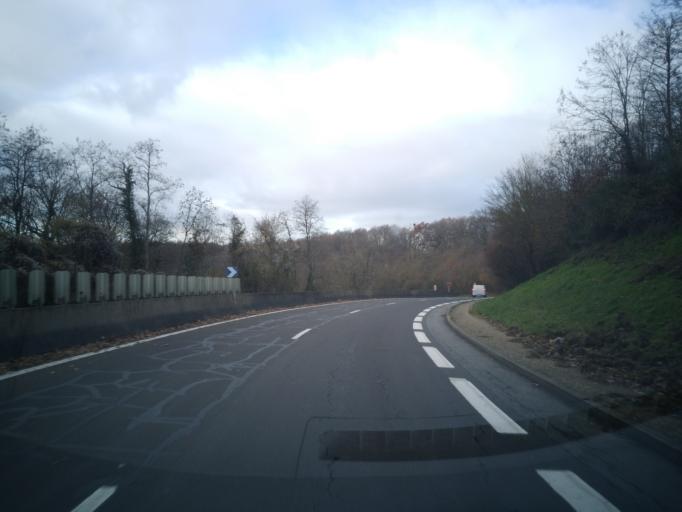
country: FR
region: Ile-de-France
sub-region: Departement des Yvelines
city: Buc
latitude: 48.7795
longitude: 2.1005
